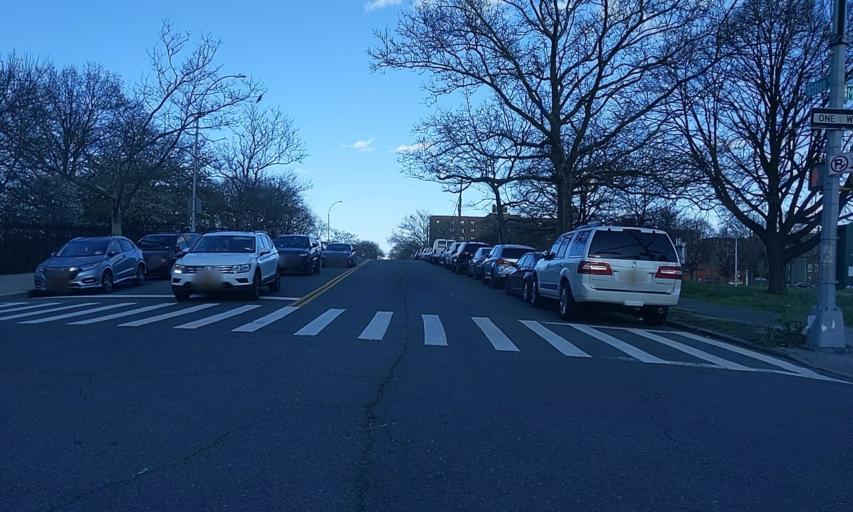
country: US
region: New York
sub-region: Bronx
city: The Bronx
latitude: 40.8267
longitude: -73.8739
